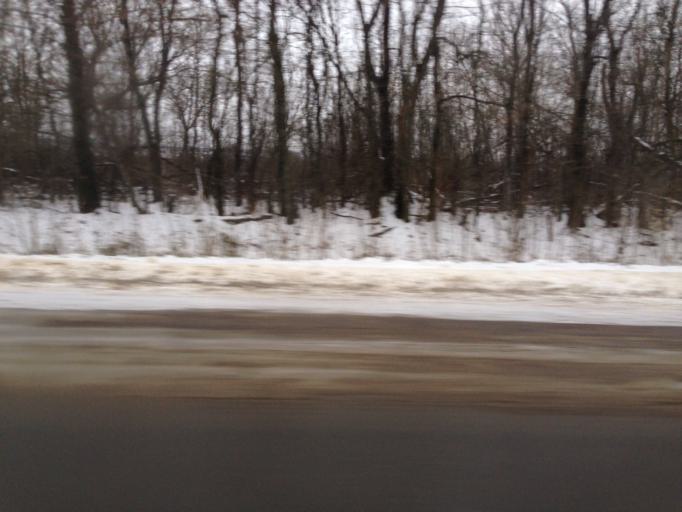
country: RU
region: Tula
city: Bolokhovo
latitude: 54.0485
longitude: 37.8341
